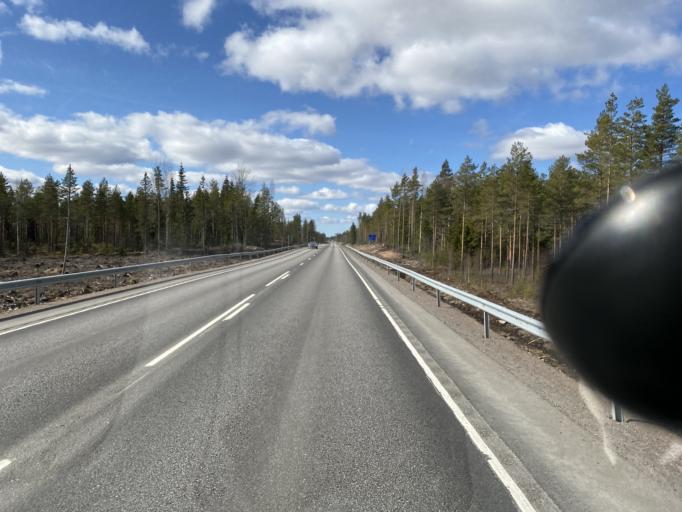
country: FI
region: Satakunta
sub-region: Pori
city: Kokemaeki
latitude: 61.1667
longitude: 22.4219
